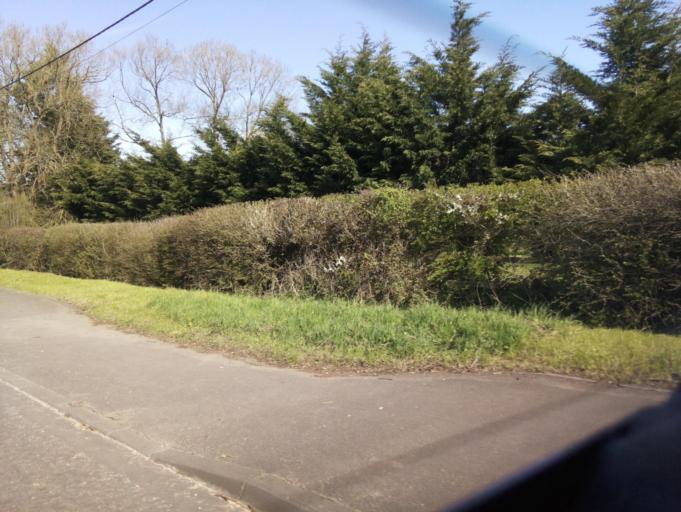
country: GB
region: England
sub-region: Wiltshire
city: Bradford-on-Avon
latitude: 51.3328
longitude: -2.2362
